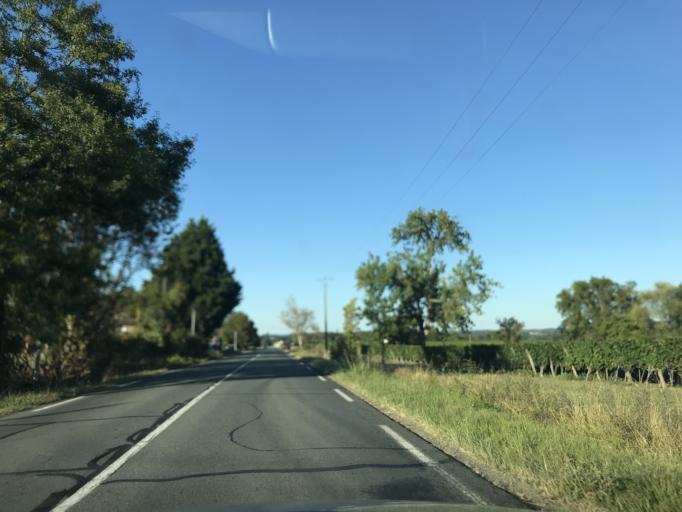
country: FR
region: Aquitaine
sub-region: Departement de la Gironde
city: Sauveterre-de-Guyenne
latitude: 44.6450
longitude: -0.1268
